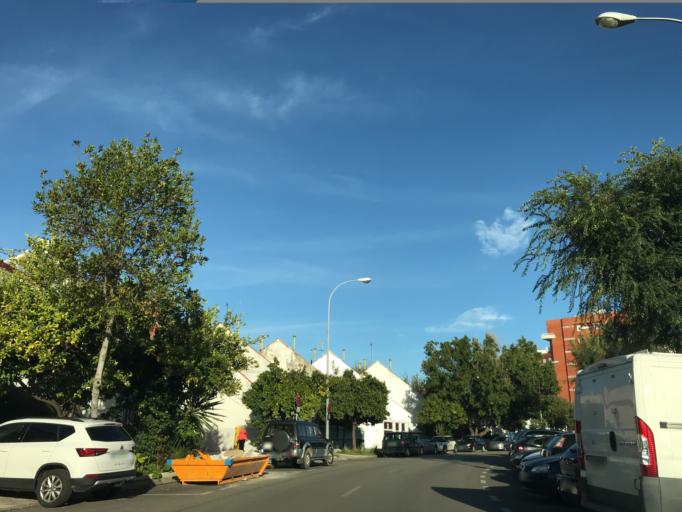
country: ES
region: Andalusia
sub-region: Provincia de Sevilla
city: Sevilla
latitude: 37.4006
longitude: -5.9295
